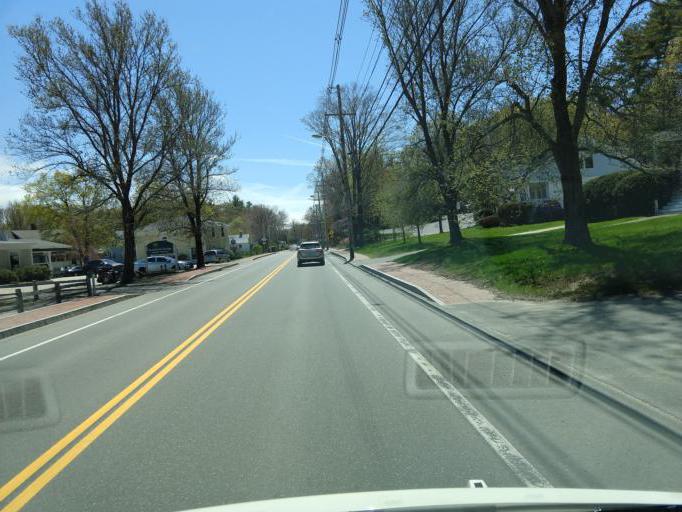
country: US
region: Maine
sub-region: York County
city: Ogunquit
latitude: 43.2469
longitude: -70.6008
